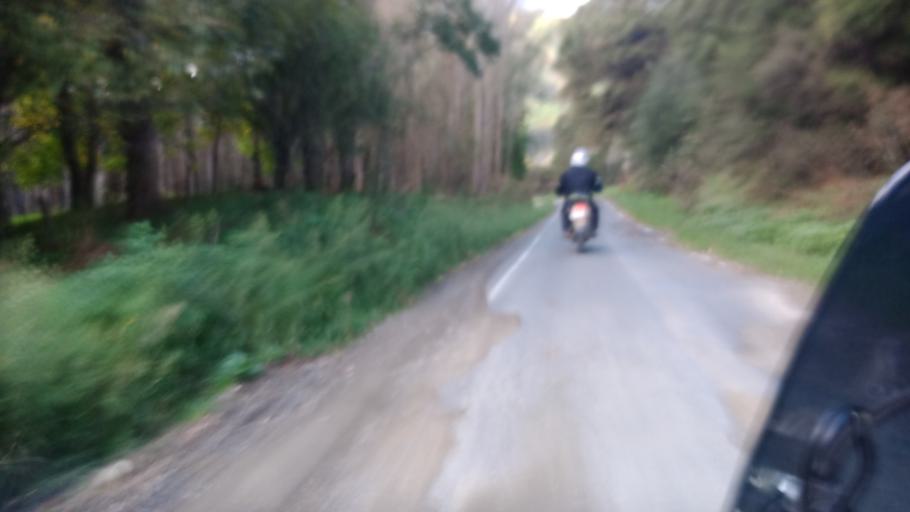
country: NZ
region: Gisborne
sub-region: Gisborne District
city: Gisborne
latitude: -38.4597
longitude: 177.6403
